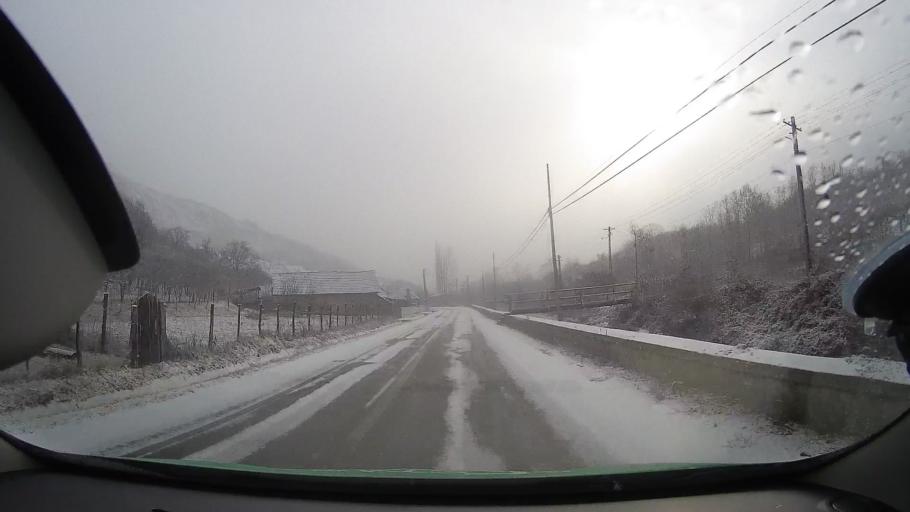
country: RO
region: Alba
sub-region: Comuna Livezile
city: Livezile
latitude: 46.3630
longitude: 23.6089
